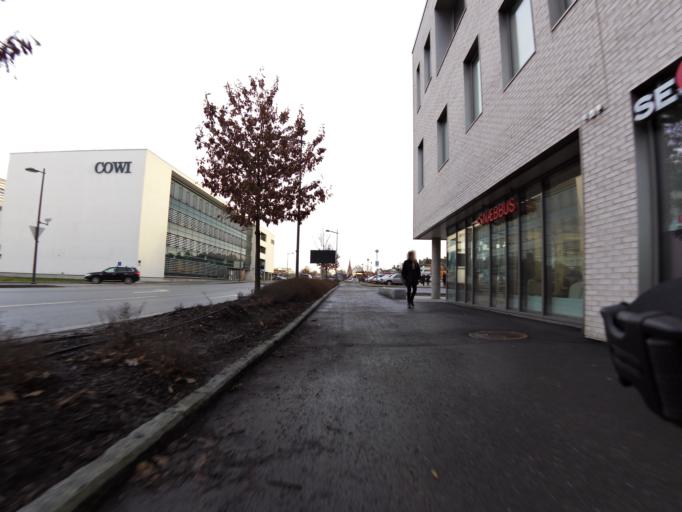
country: NO
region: Ostfold
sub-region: Fredrikstad
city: Fredrikstad
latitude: 59.2119
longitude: 10.9282
